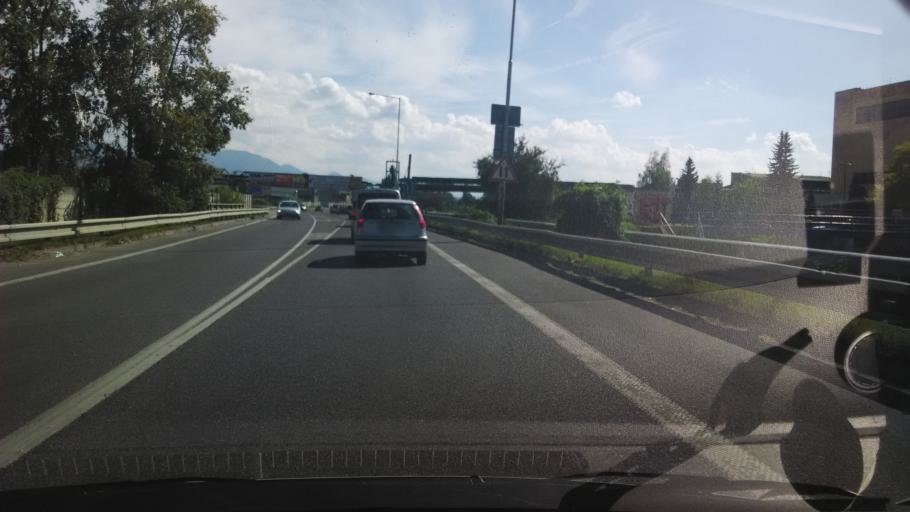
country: SK
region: Zilinsky
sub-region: Okres Martin
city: Martin
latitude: 49.0610
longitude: 18.9092
